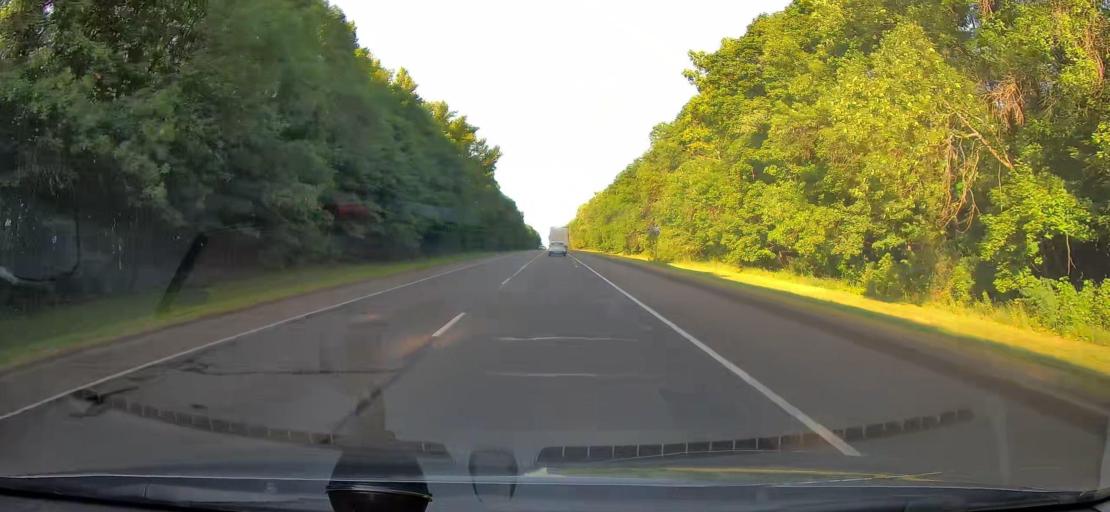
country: RU
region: Tula
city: Chern'
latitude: 53.4820
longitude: 36.9921
